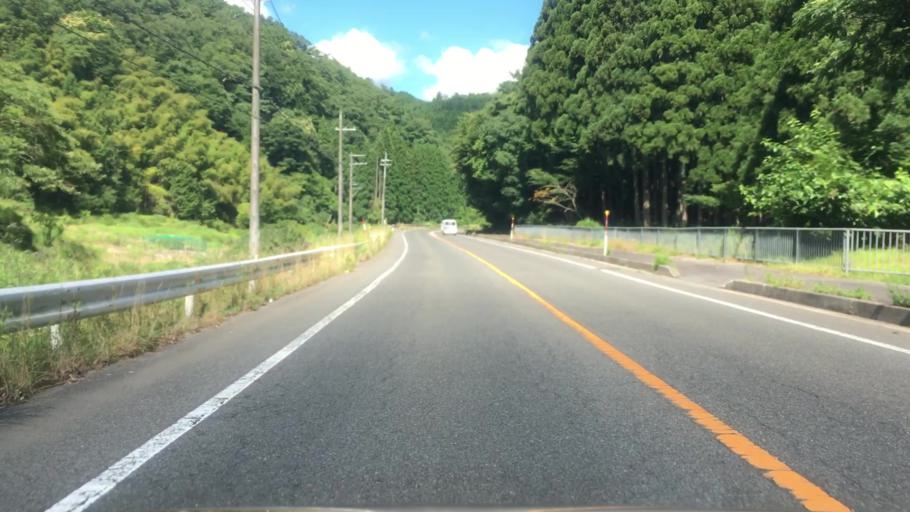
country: JP
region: Hyogo
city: Toyooka
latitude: 35.5761
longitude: 134.7573
